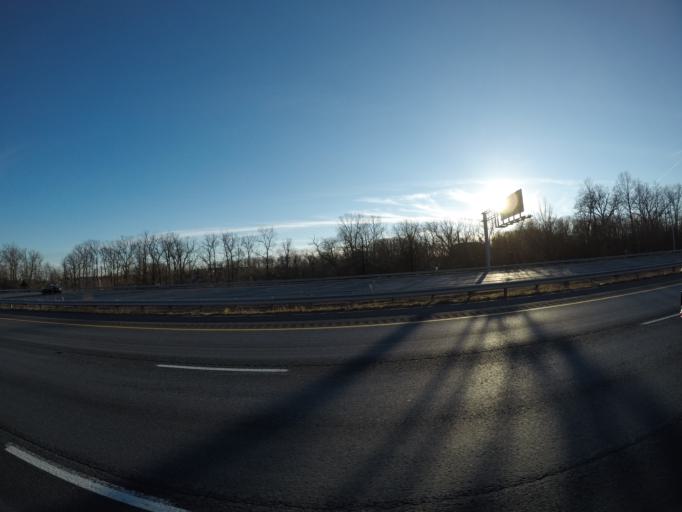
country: US
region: Maryland
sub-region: Howard County
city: Columbia
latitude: 39.2225
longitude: -76.8041
